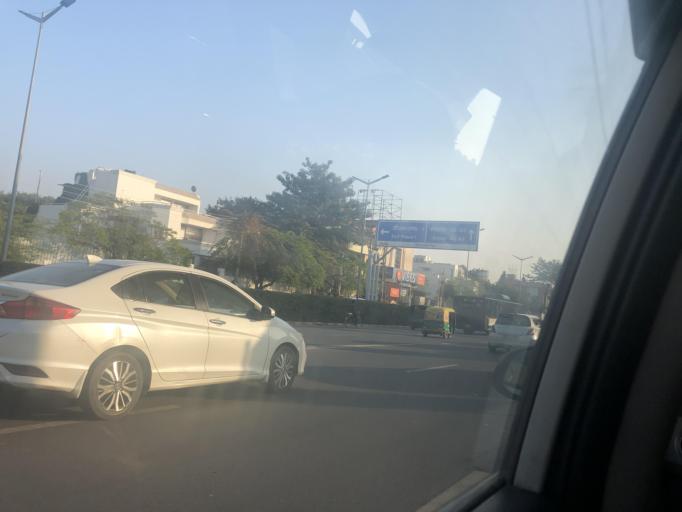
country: IN
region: Haryana
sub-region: Gurgaon
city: Gurgaon
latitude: 28.4740
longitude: 77.0940
